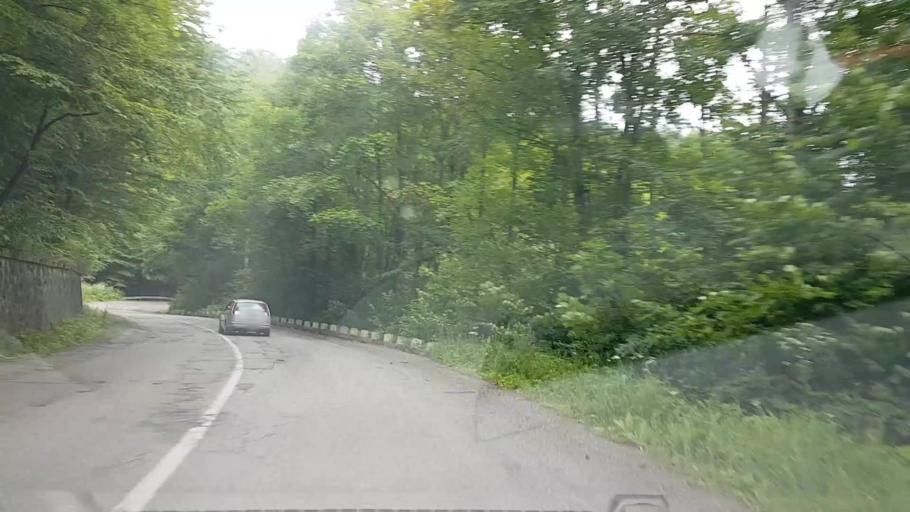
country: RO
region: Neamt
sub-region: Comuna Pangarati
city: Pangarati
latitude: 46.9465
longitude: 26.1301
